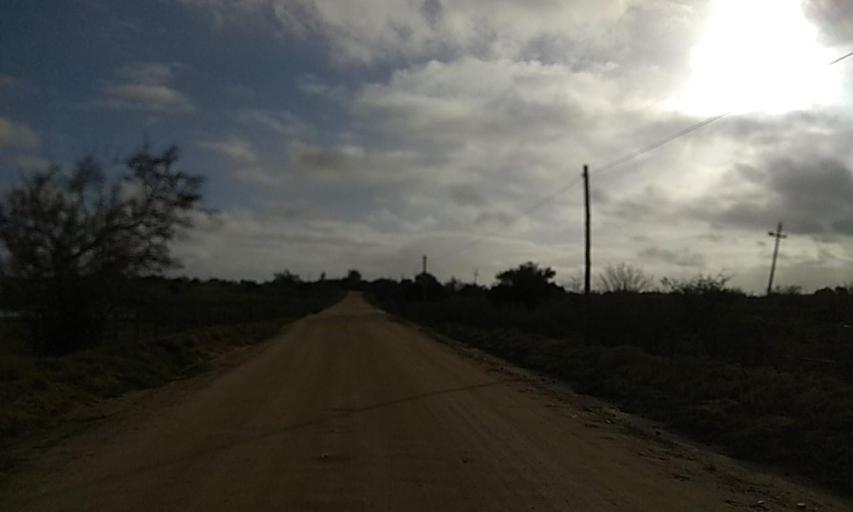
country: UY
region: Florida
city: Florida
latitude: -34.0577
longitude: -56.1911
